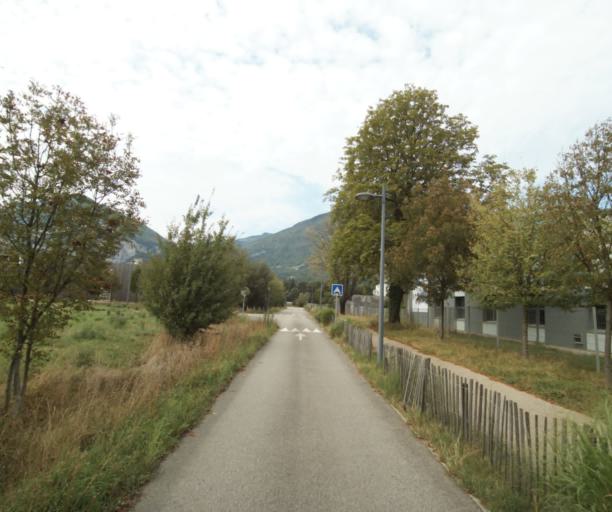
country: FR
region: Rhone-Alpes
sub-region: Departement de l'Isere
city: Saint-Egreve
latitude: 45.2283
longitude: 5.6715
